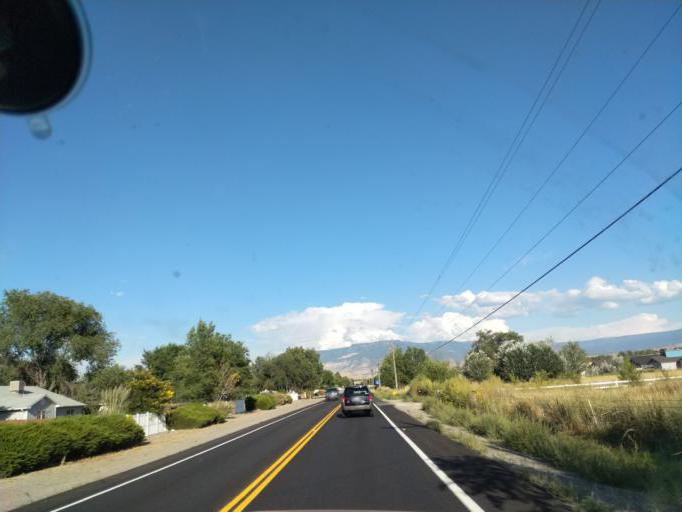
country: US
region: Colorado
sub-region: Mesa County
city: Fruitvale
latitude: 39.0629
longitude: -108.4732
